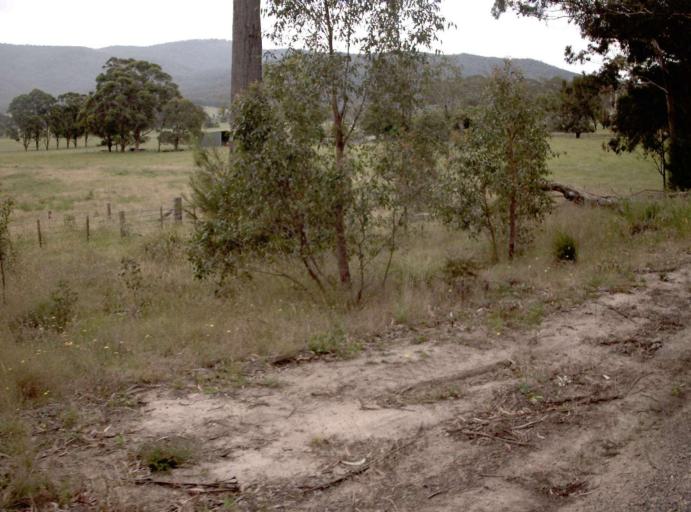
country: AU
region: New South Wales
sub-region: Bombala
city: Bombala
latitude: -37.4917
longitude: 149.1821
